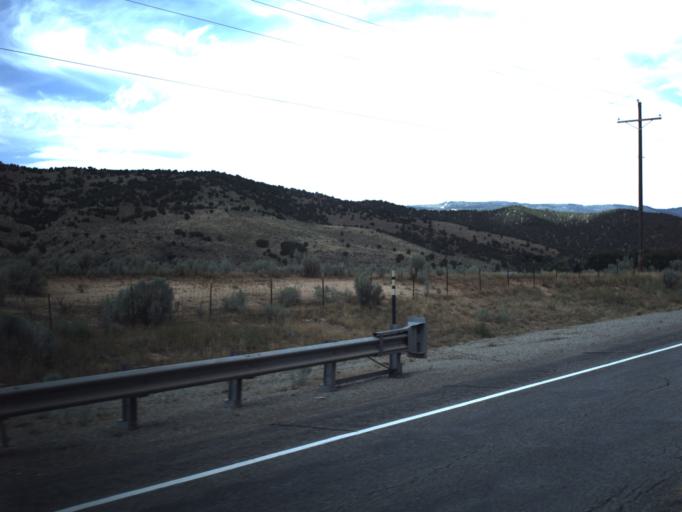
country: US
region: Utah
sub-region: Utah County
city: Woodland Hills
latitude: 39.8661
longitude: -111.5316
